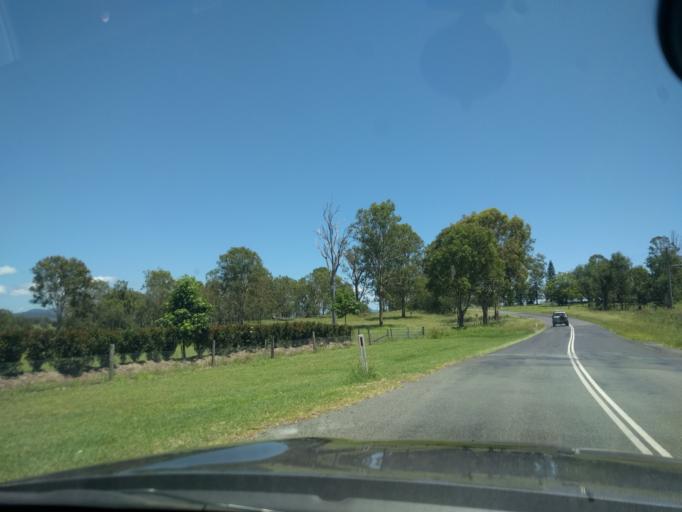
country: AU
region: Queensland
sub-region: Logan
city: Cedar Vale
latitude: -28.0080
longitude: 153.0112
